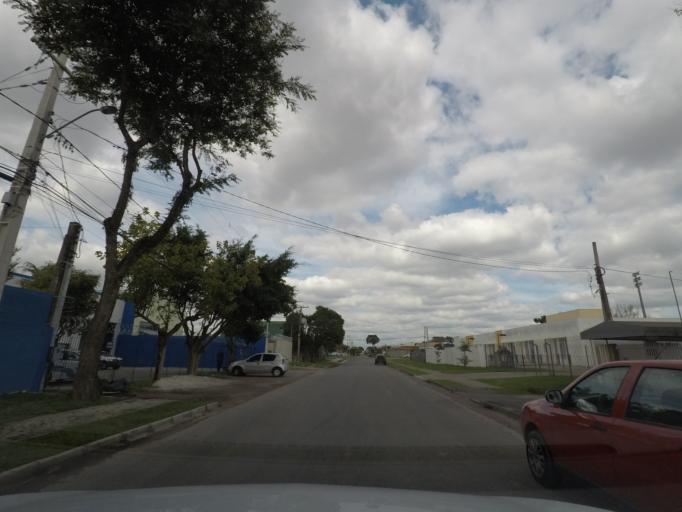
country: BR
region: Parana
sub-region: Sao Jose Dos Pinhais
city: Sao Jose dos Pinhais
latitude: -25.4894
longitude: -49.2380
